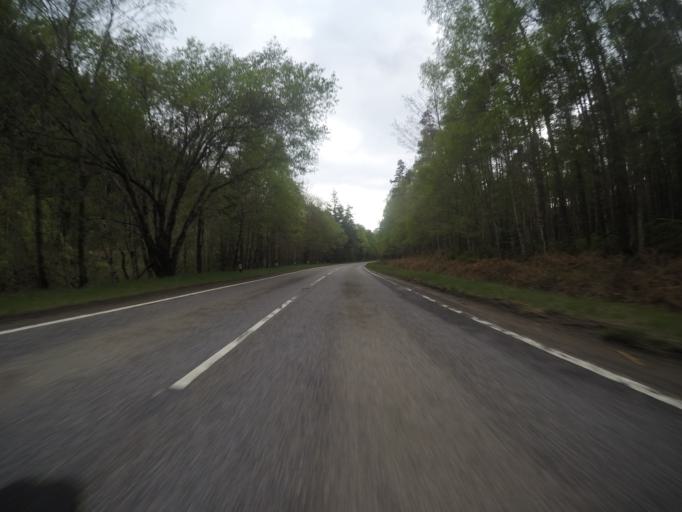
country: GB
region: Scotland
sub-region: Highland
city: Beauly
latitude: 57.2115
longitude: -4.6770
